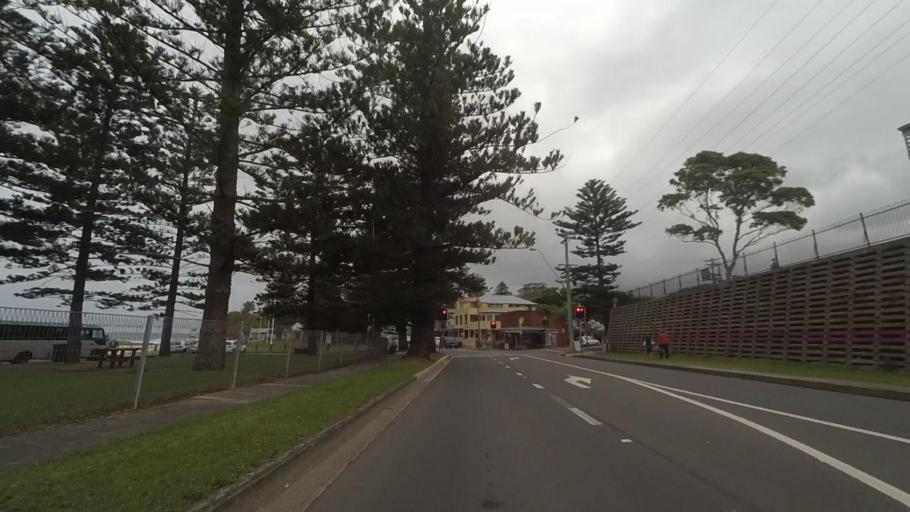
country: AU
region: New South Wales
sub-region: Wollongong
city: Bulli
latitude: -34.3059
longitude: 150.9349
